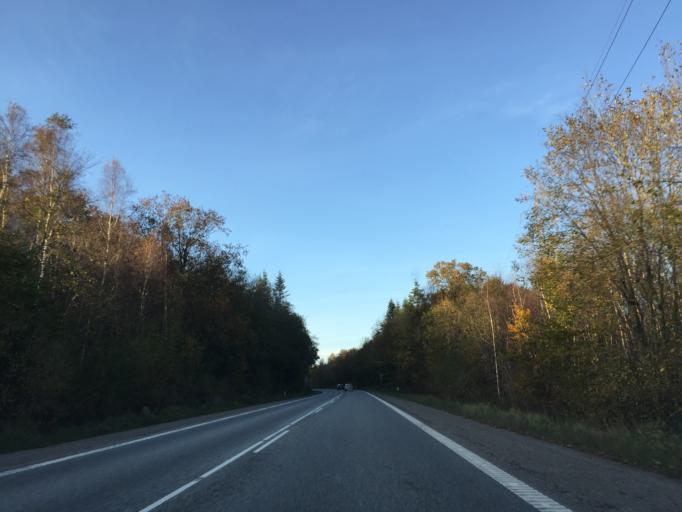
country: DK
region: South Denmark
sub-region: Aabenraa Kommune
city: Krusa
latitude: 54.8645
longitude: 9.4017
